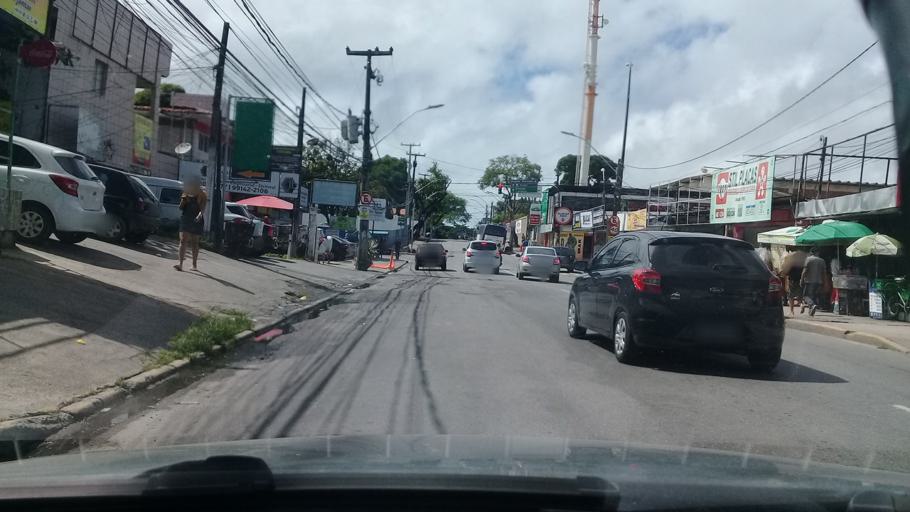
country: BR
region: Pernambuco
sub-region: Jaboatao Dos Guararapes
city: Jaboatao
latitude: -8.1649
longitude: -34.9188
